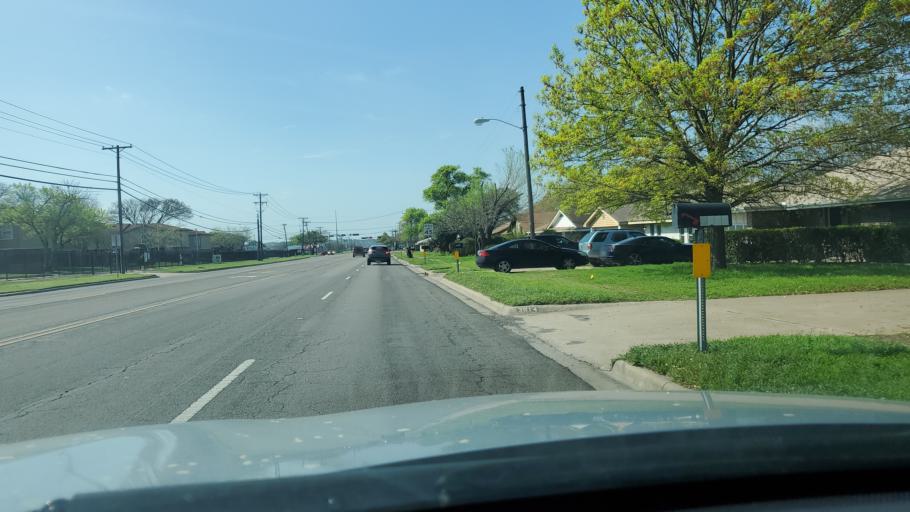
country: US
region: Texas
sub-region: Bell County
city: Temple
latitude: 31.0635
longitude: -97.3718
